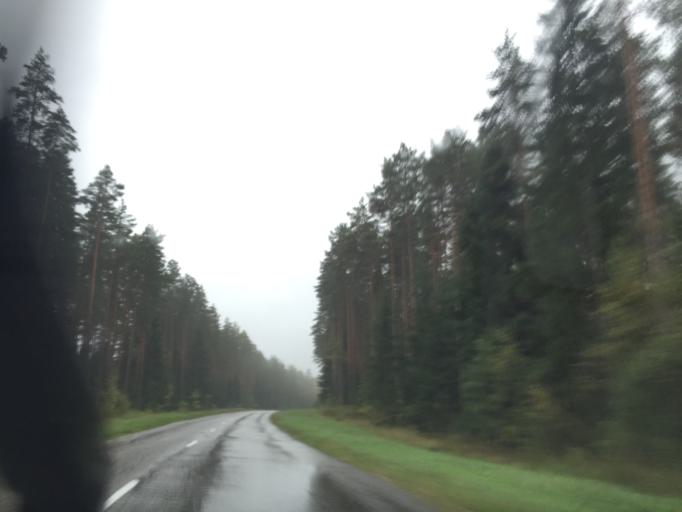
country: LV
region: Ropazu
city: Ropazi
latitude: 57.0234
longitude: 24.6829
